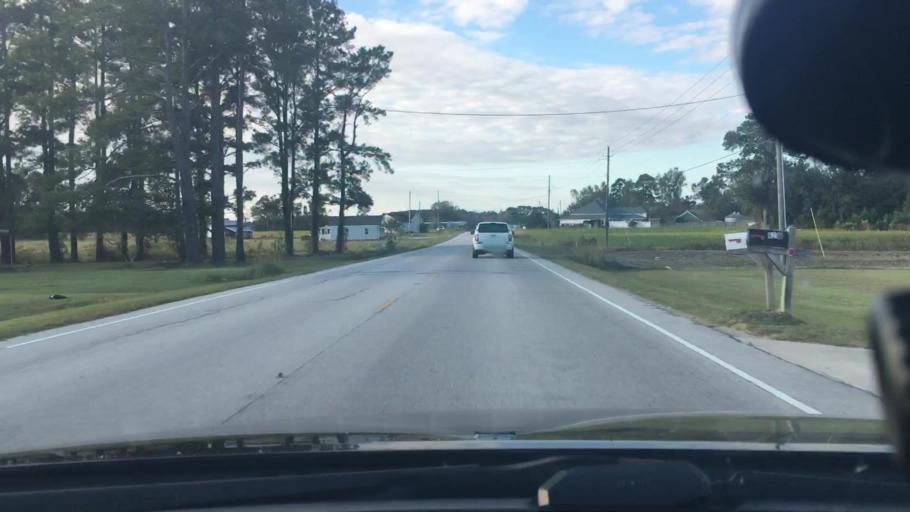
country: US
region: North Carolina
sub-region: Pitt County
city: Windsor
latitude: 35.4969
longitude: -77.3104
